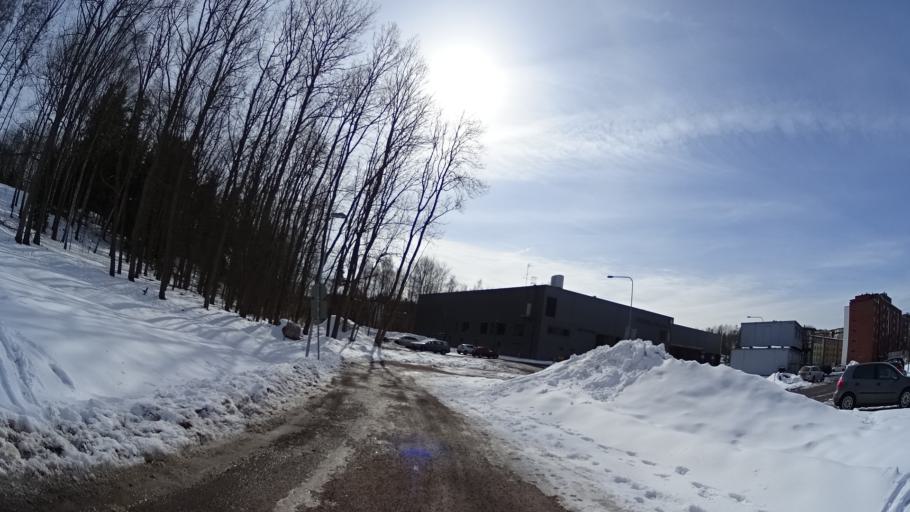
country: FI
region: Uusimaa
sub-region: Helsinki
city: Kauniainen
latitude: 60.2073
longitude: 24.7125
